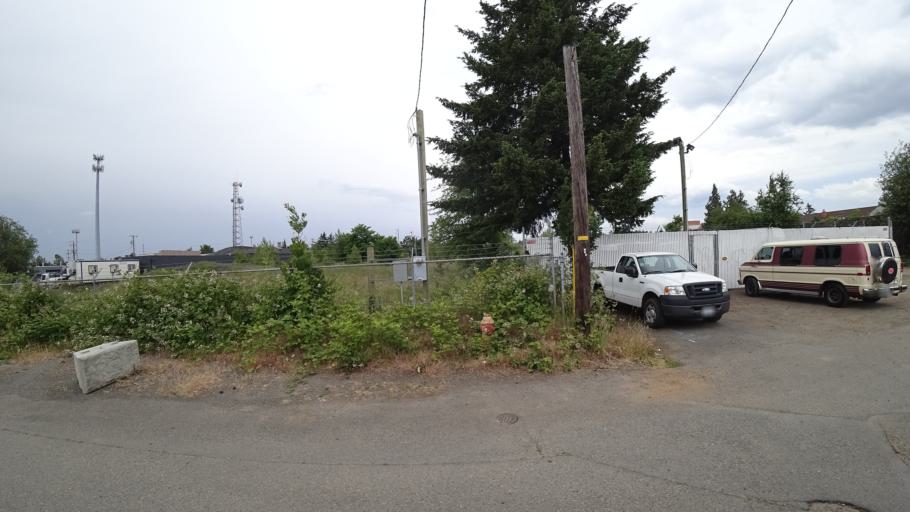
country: US
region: Oregon
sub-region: Multnomah County
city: Lents
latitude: 45.5204
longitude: -122.5601
